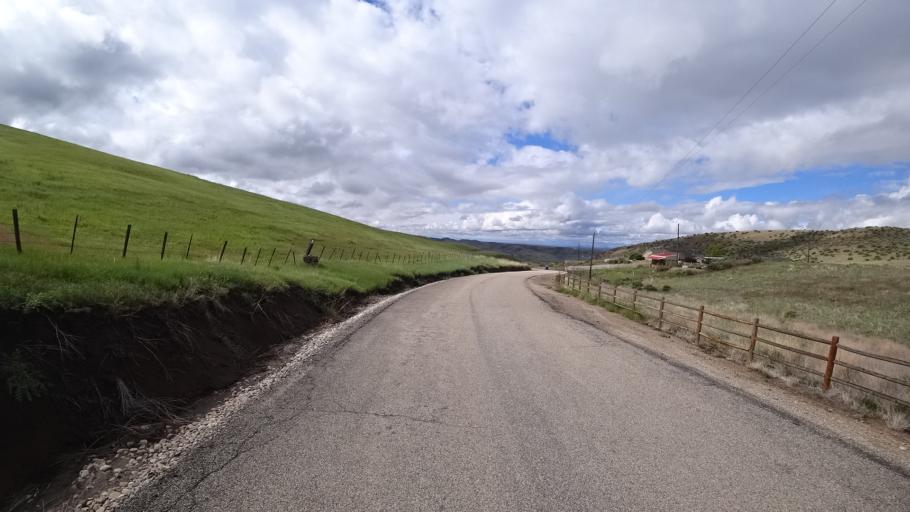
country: US
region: Idaho
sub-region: Ada County
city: Garden City
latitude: 43.7389
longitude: -116.2263
